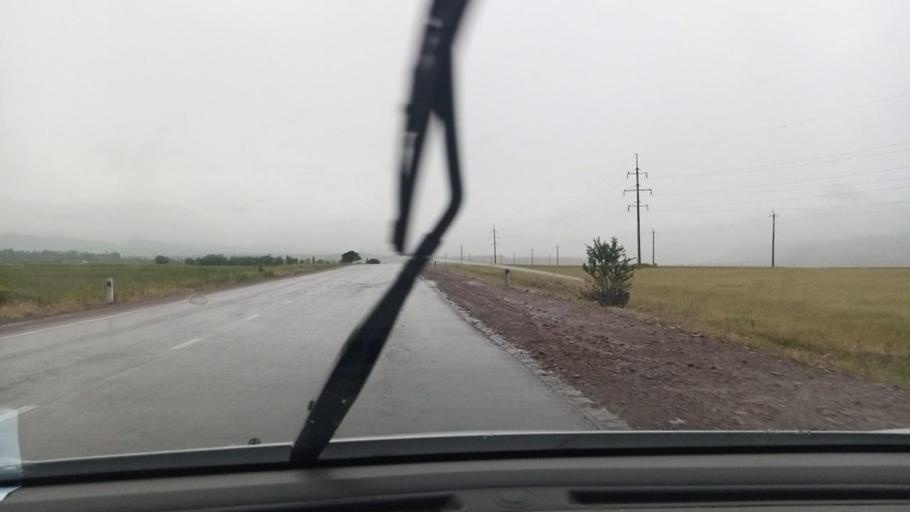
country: UZ
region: Toshkent
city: Angren
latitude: 41.0350
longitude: 70.1433
